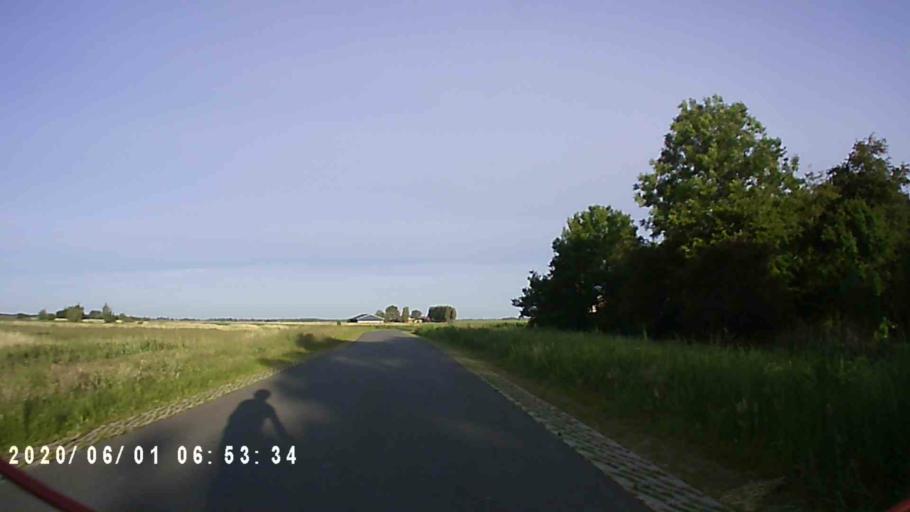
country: NL
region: Friesland
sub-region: Gemeente Kollumerland en Nieuwkruisland
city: Kollum
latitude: 53.3118
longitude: 6.1282
